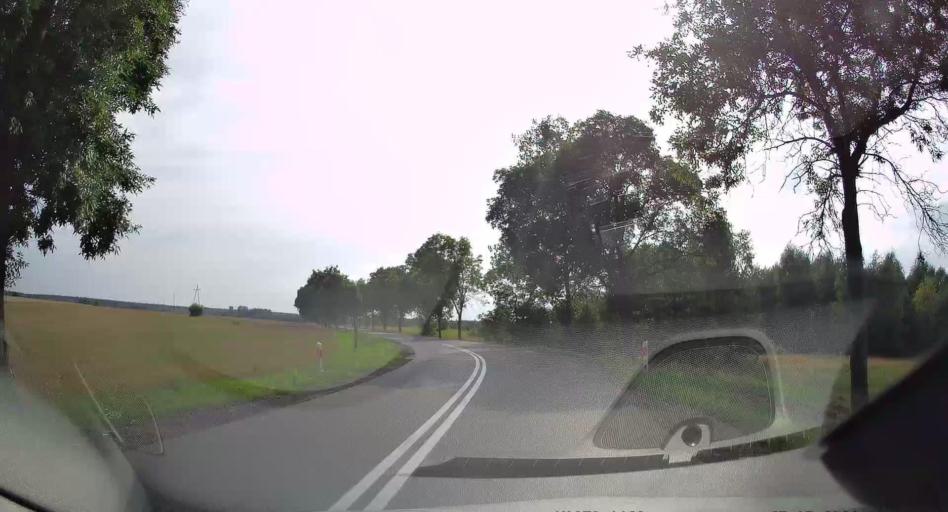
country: PL
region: Lodz Voivodeship
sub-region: Powiat tomaszowski
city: Rzeczyca
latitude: 51.5628
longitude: 20.2669
